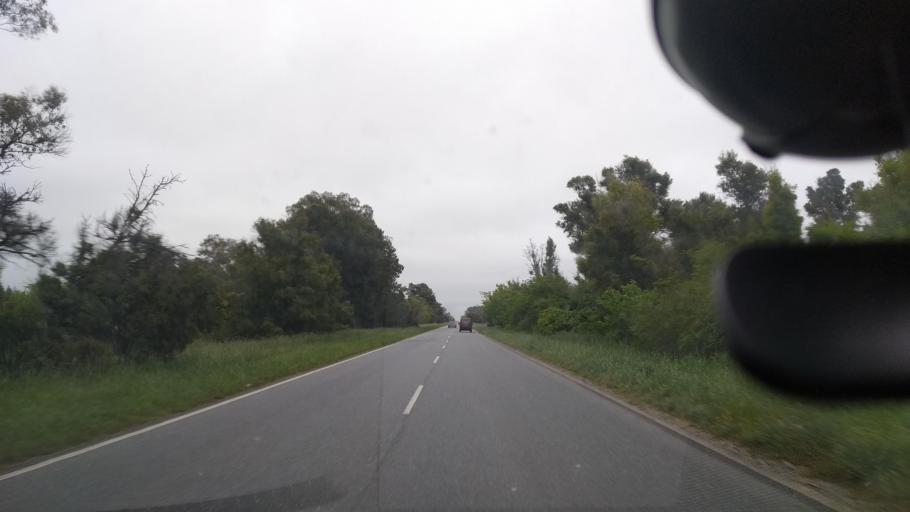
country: AR
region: Buenos Aires
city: Veronica
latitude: -35.3162
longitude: -57.4832
